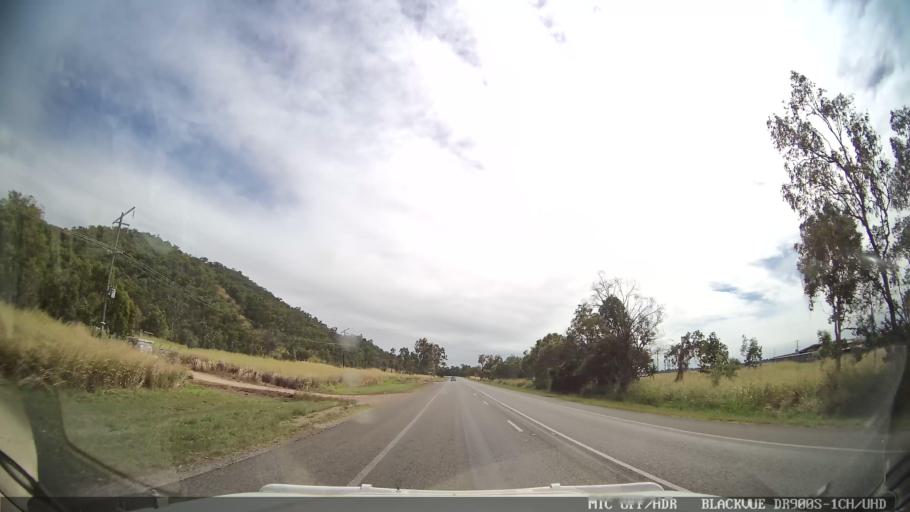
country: AU
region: Queensland
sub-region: Hinchinbrook
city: Ingham
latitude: -19.0148
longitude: 146.3658
